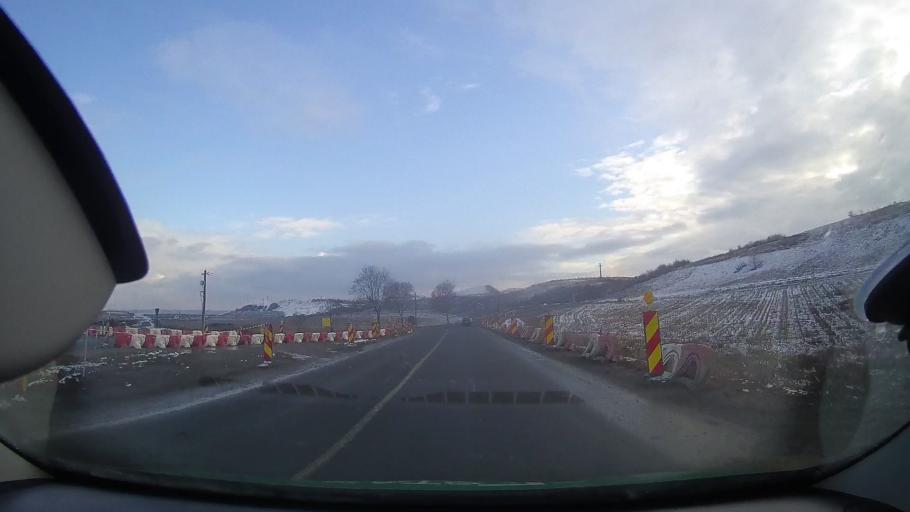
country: RO
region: Mures
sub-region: Comuna Iernut
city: Iernut
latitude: 46.4300
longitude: 24.2587
